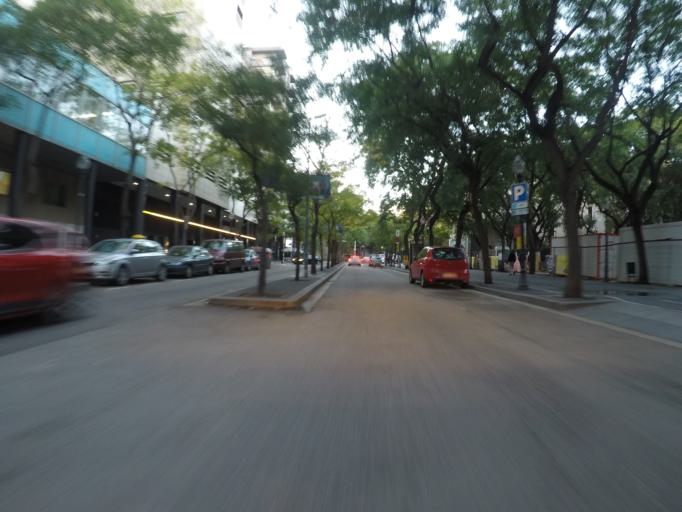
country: ES
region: Catalonia
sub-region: Provincia de Barcelona
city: Ciutat Vella
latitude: 41.3767
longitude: 2.1732
